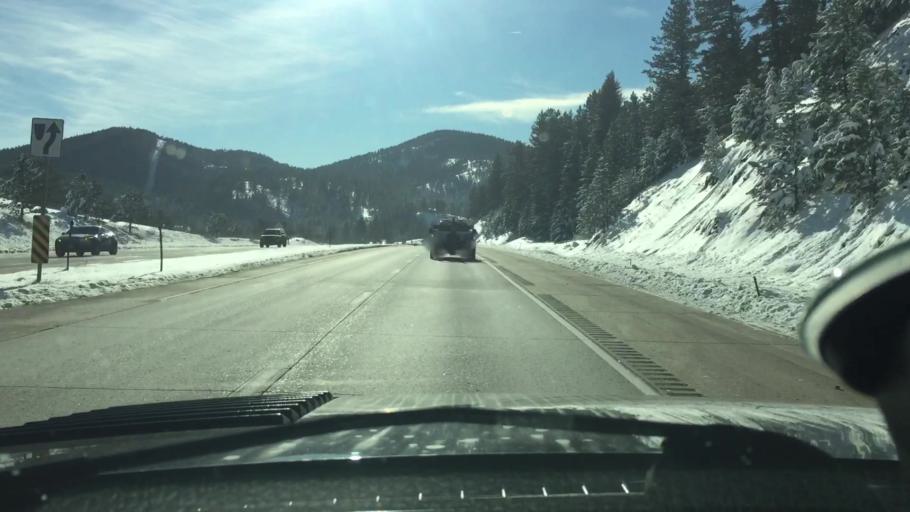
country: US
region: Colorado
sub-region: Jefferson County
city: Indian Hills
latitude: 39.5986
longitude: -105.2263
